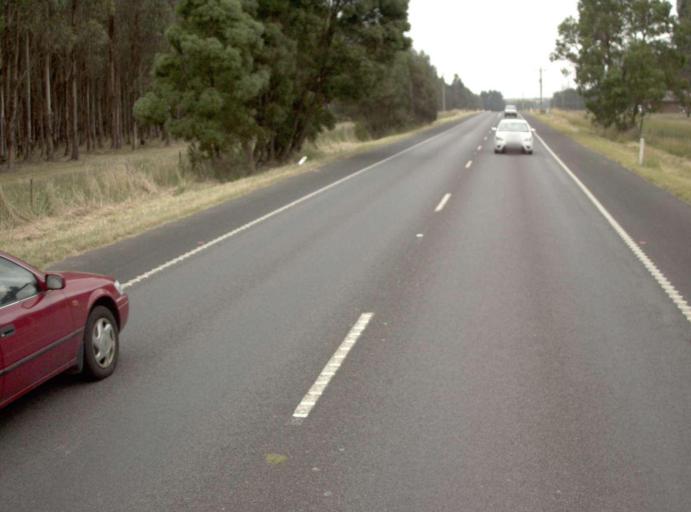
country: AU
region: Victoria
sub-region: Latrobe
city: Morwell
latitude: -38.2905
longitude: 146.4149
